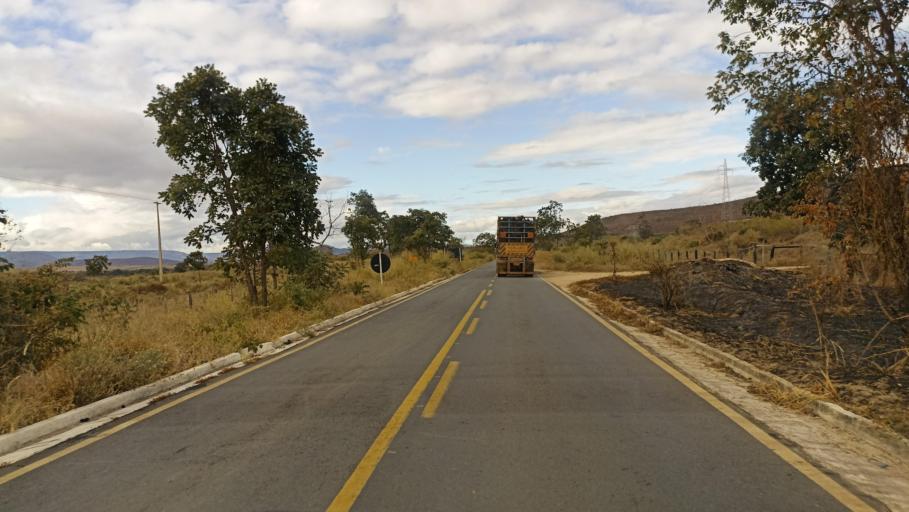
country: BR
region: Minas Gerais
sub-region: Itinga
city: Itinga
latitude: -16.5974
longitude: -41.7075
